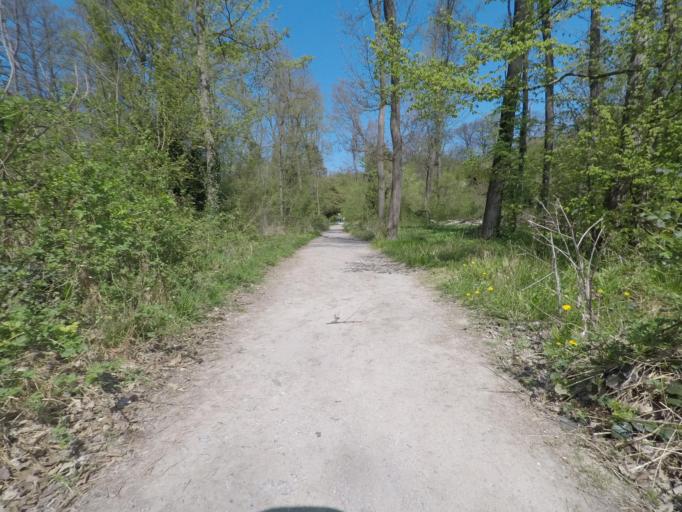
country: AT
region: Lower Austria
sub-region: Politischer Bezirk Modling
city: Perchtoldsdorf
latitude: 48.1708
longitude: 16.2480
